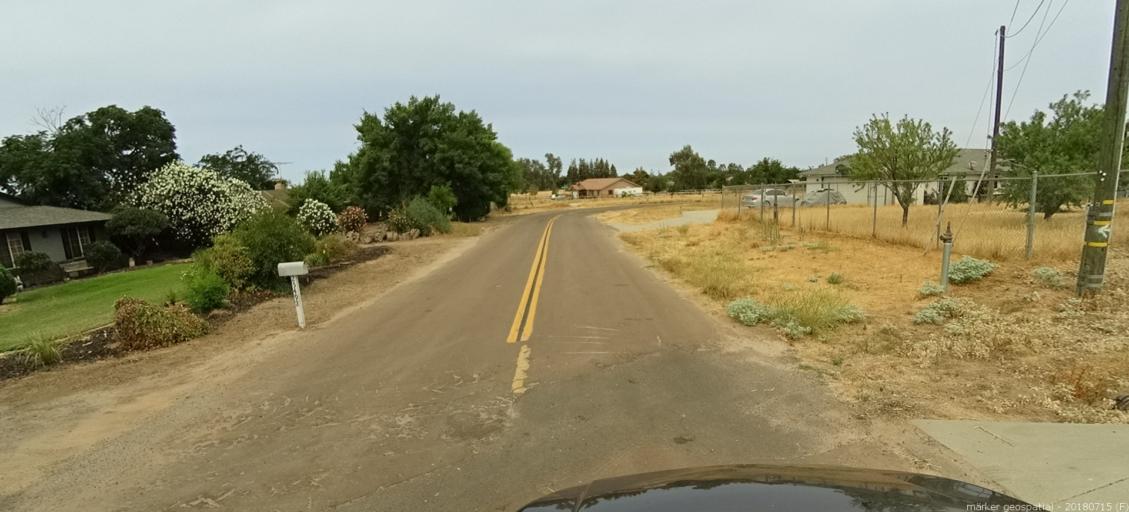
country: US
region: California
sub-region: Madera County
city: Madera Acres
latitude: 37.0164
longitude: -120.0833
